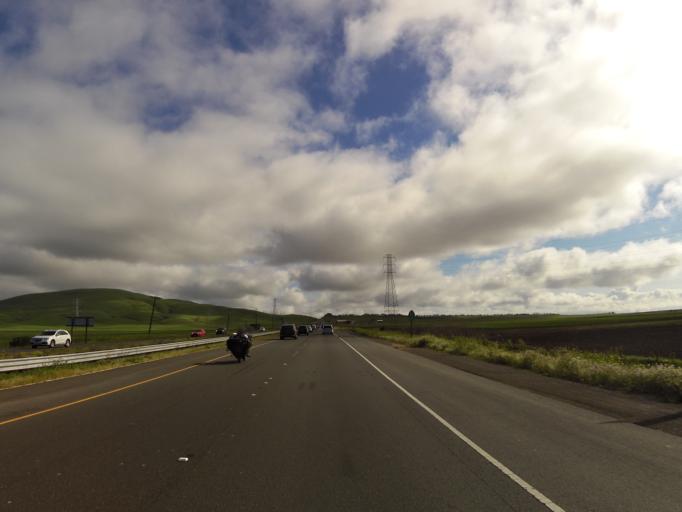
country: US
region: California
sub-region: Marin County
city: Black Point-Green Point
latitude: 38.1350
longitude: -122.4745
